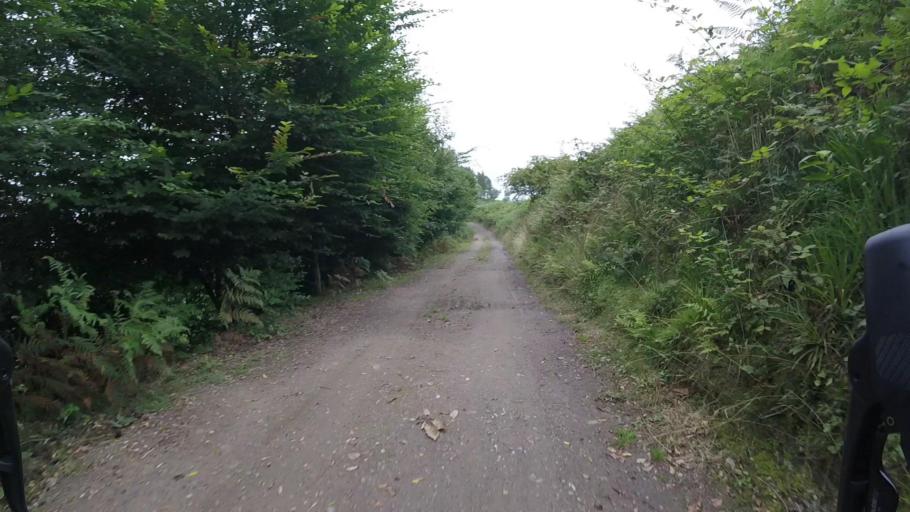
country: ES
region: Navarre
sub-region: Provincia de Navarra
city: Arano
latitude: 43.2538
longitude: -1.8873
